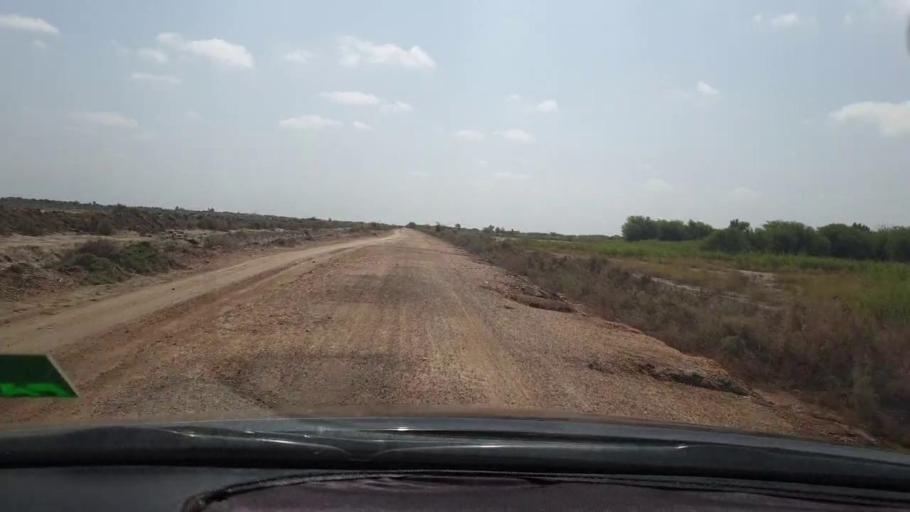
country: PK
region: Sindh
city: Tando Bago
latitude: 24.8338
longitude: 69.0541
